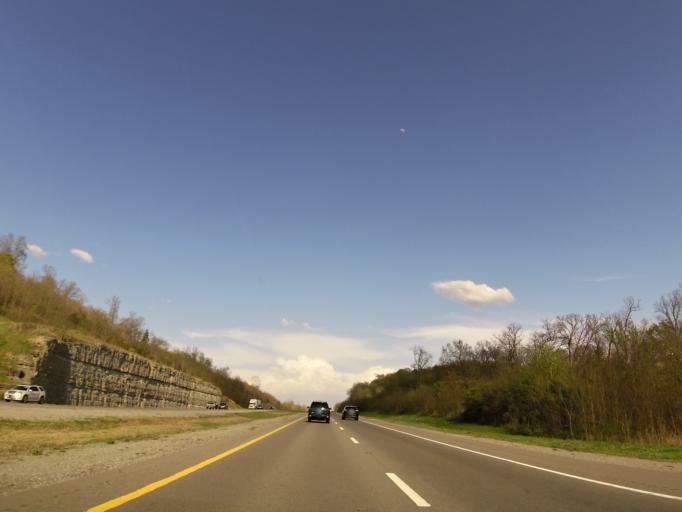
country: US
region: Tennessee
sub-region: Williamson County
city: Thompson's Station
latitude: 35.8226
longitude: -86.9332
